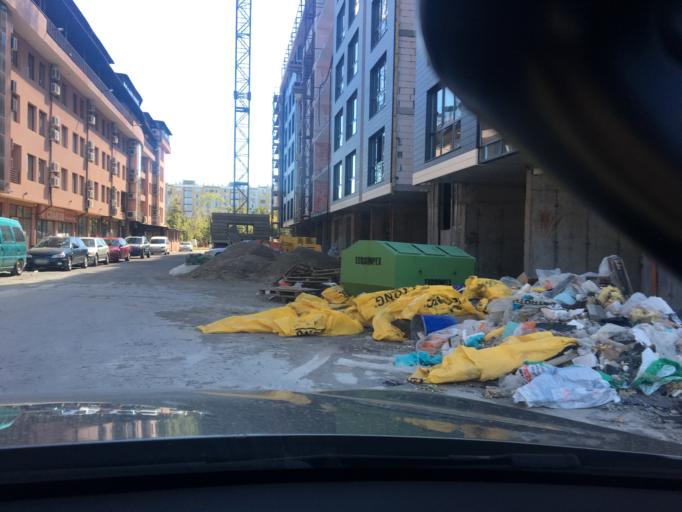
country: BG
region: Burgas
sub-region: Obshtina Burgas
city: Burgas
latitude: 42.5291
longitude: 27.4536
